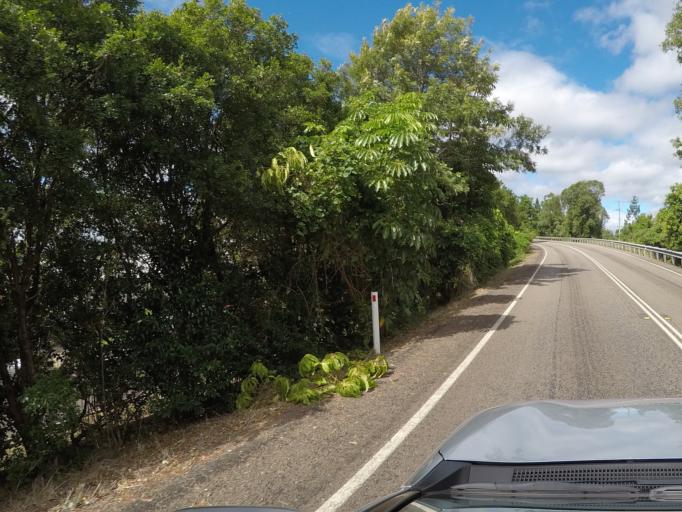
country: AU
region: Queensland
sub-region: Sunshine Coast
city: Nambour
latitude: -26.6364
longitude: 152.8697
